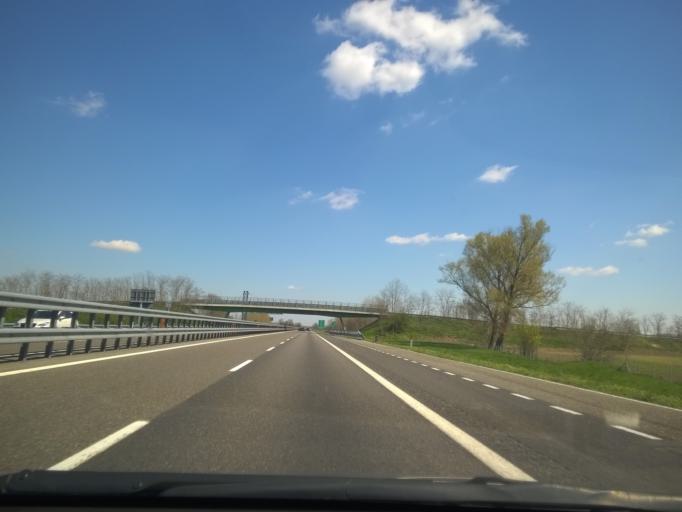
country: IT
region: Emilia-Romagna
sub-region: Provincia di Piacenza
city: Castel San Giovanni
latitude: 45.0742
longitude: 9.4622
